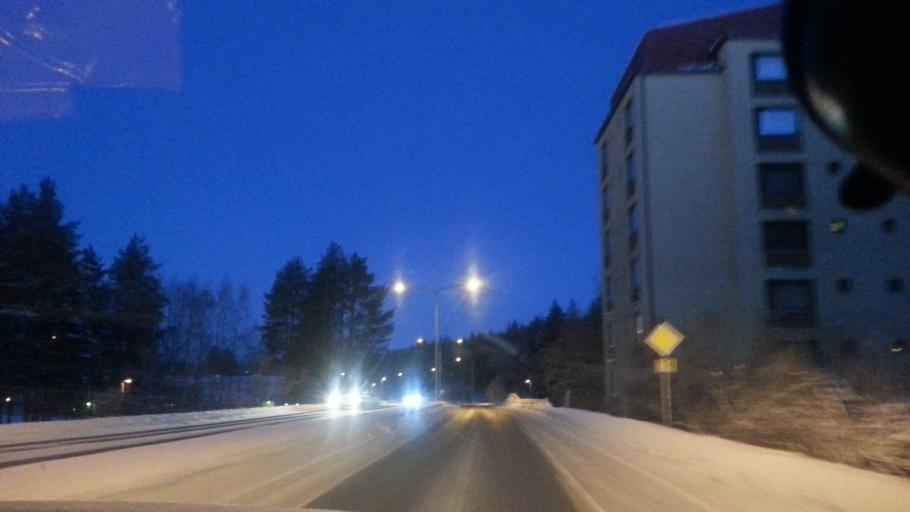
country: FI
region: Lapland
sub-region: Rovaniemi
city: Rovaniemi
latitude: 66.4982
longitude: 25.7564
